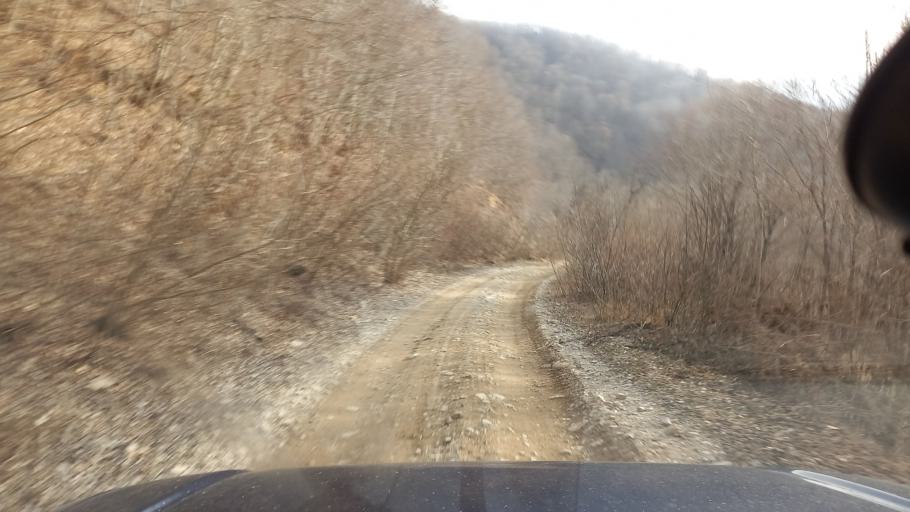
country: RU
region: Adygeya
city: Kamennomostskiy
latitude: 44.1452
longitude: 40.3047
